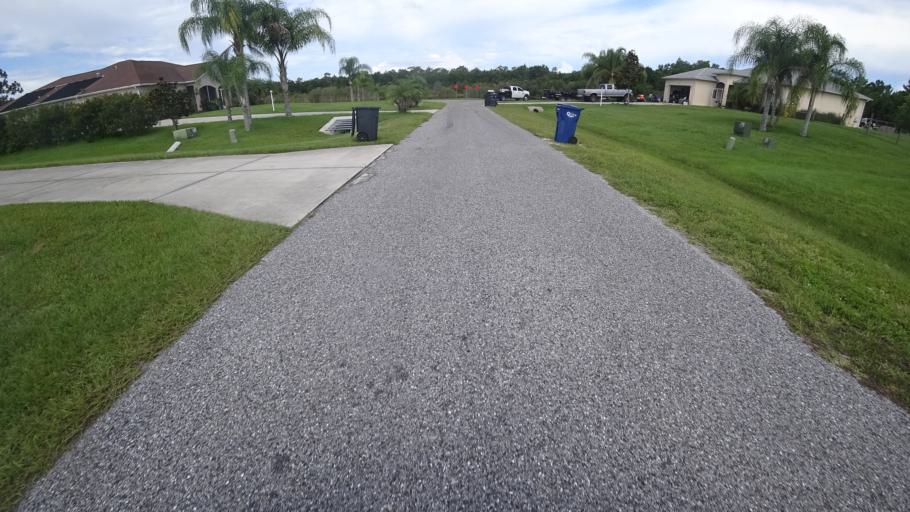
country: US
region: Florida
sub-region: Sarasota County
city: Lake Sarasota
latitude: 27.3901
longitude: -82.2767
